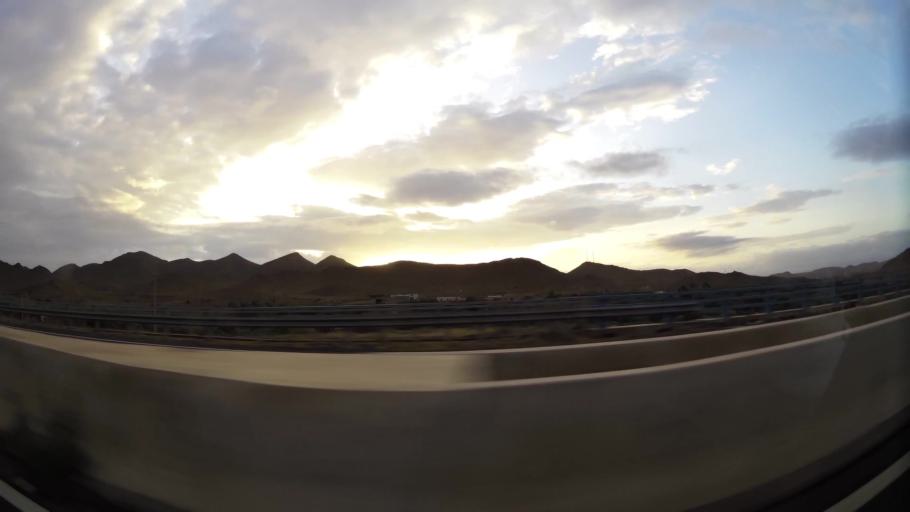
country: MA
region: Oriental
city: Taourirt
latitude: 34.4777
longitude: -2.9867
